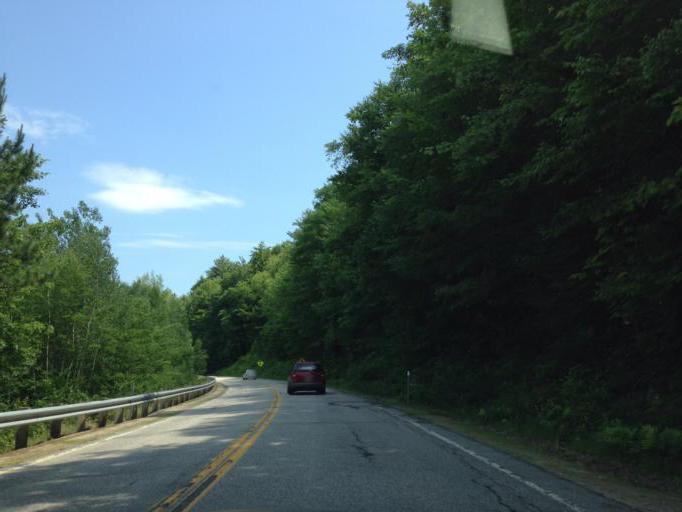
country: US
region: New Hampshire
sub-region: Carroll County
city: Conway
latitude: 43.9896
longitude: -71.1664
